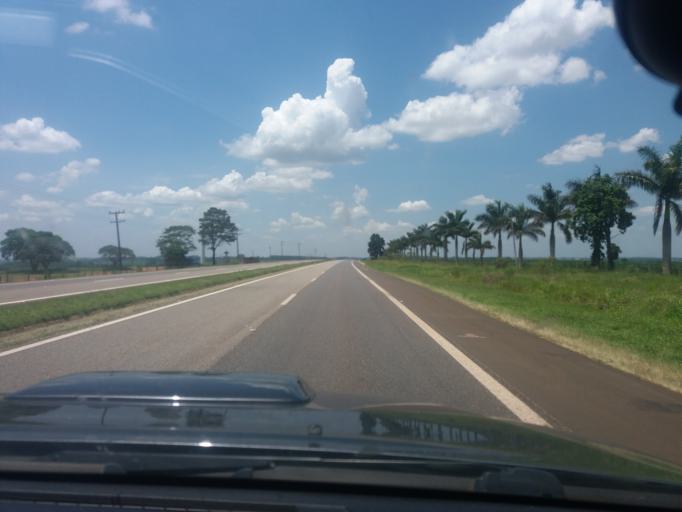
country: BR
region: Sao Paulo
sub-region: Itapetininga
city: Itapetininga
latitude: -23.5490
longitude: -47.9685
